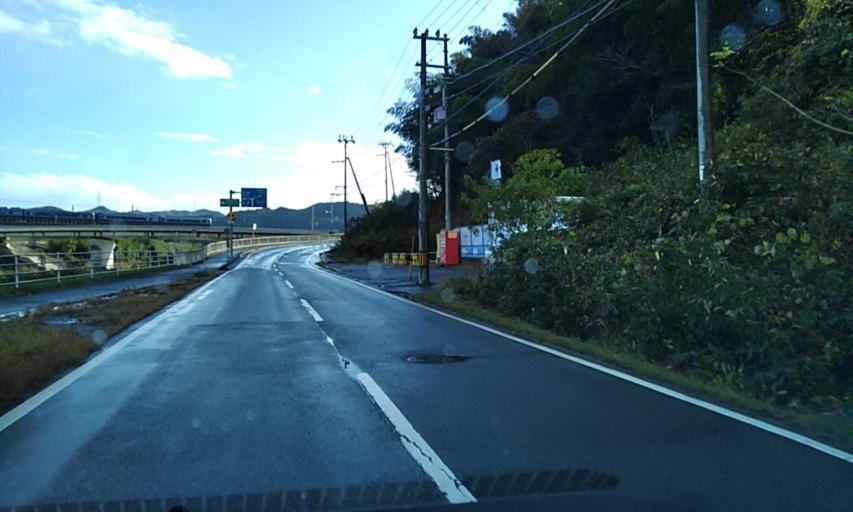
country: JP
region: Kyoto
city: Fukuchiyama
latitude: 35.3957
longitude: 135.1502
